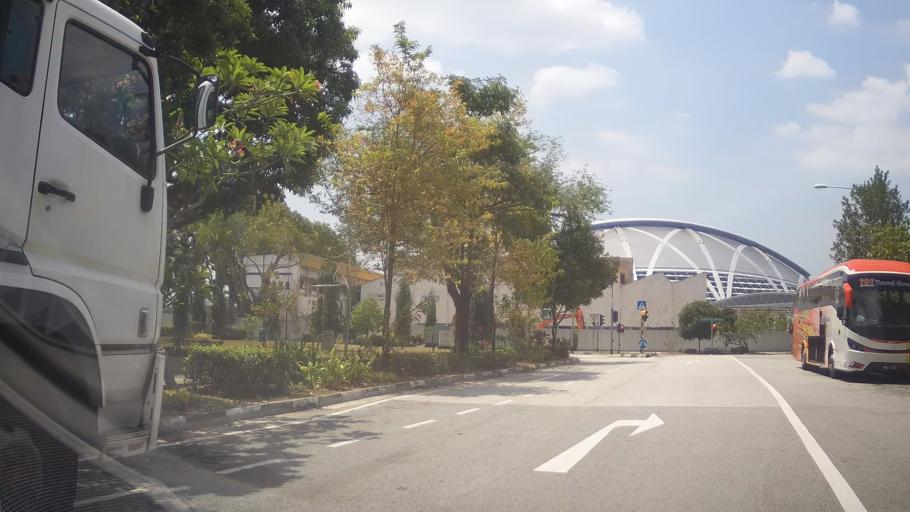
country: SG
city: Singapore
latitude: 1.3093
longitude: 103.8717
